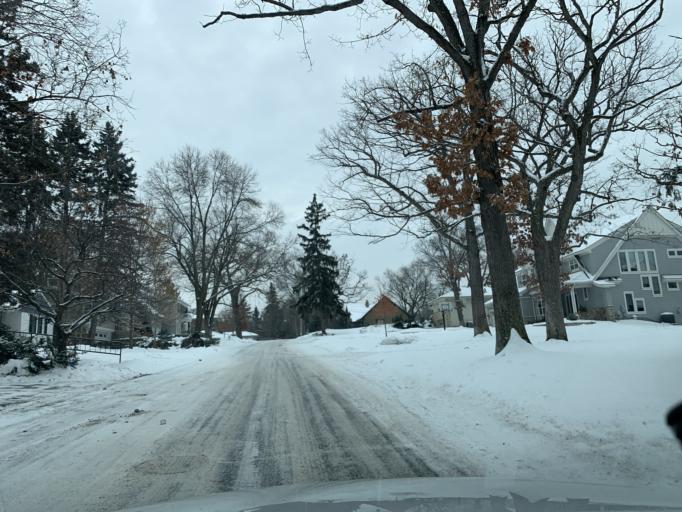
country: US
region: Minnesota
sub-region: Hennepin County
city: Edina
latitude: 44.9161
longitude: -93.3594
